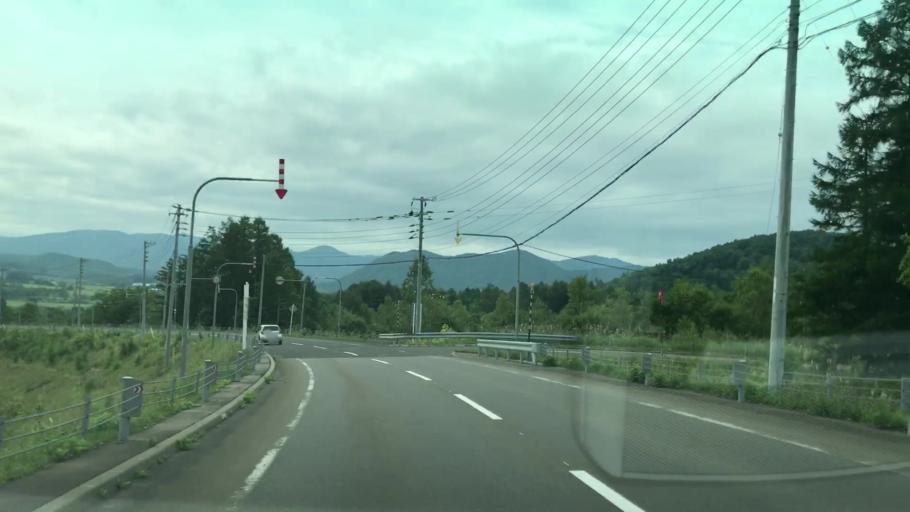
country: JP
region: Hokkaido
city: Yoichi
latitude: 43.1110
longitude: 140.8192
